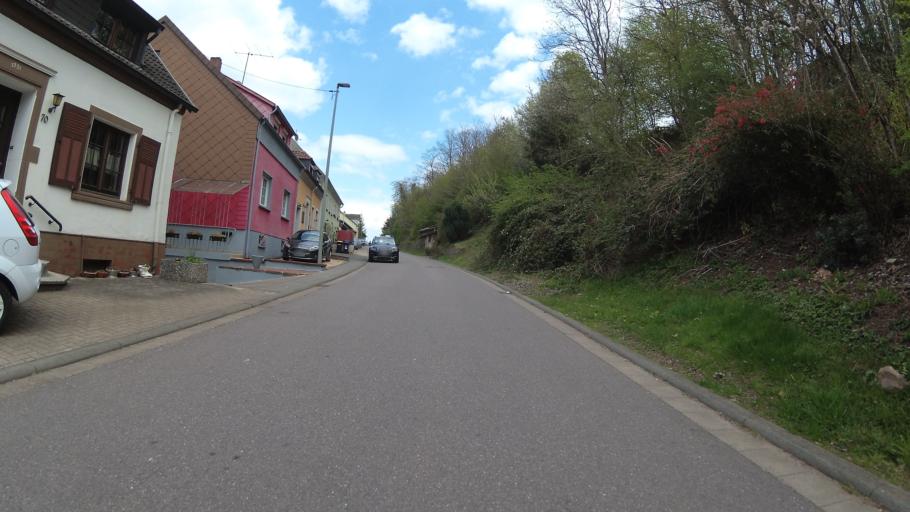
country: DE
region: Saarland
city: Schmelz
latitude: 49.4830
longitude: 6.8321
